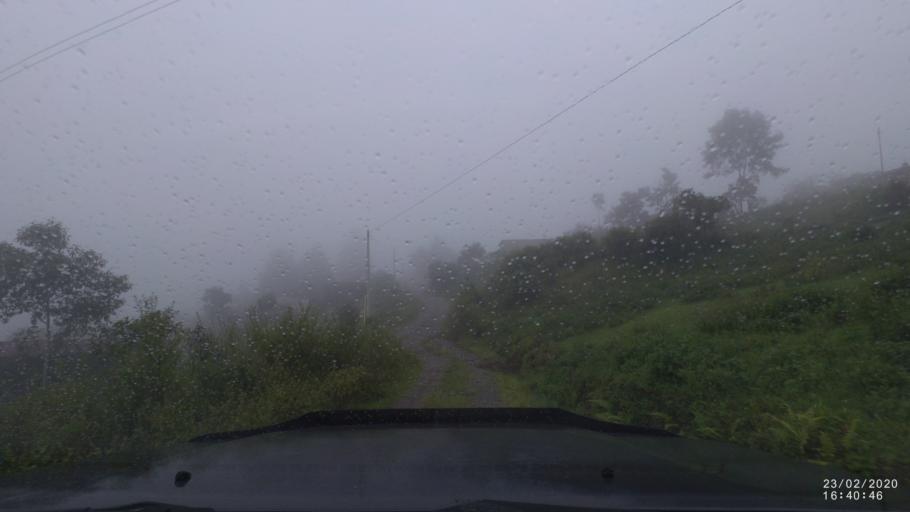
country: BO
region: Cochabamba
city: Colomi
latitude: -17.0839
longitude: -66.0024
